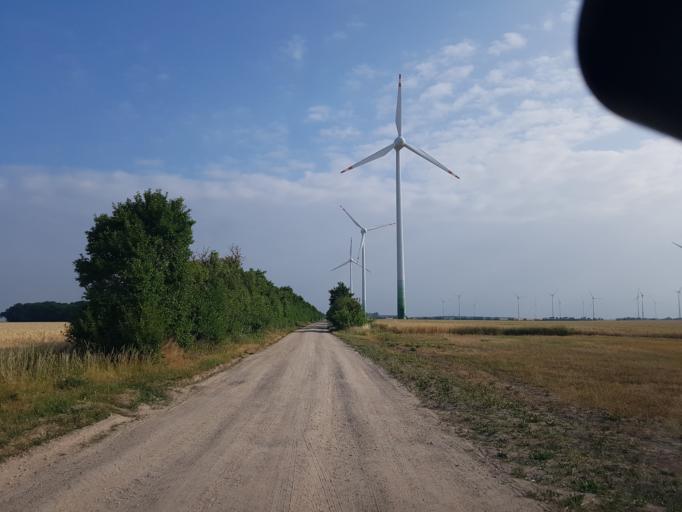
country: DE
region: Saxony-Anhalt
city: Kropstadt
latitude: 51.9958
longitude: 12.8179
